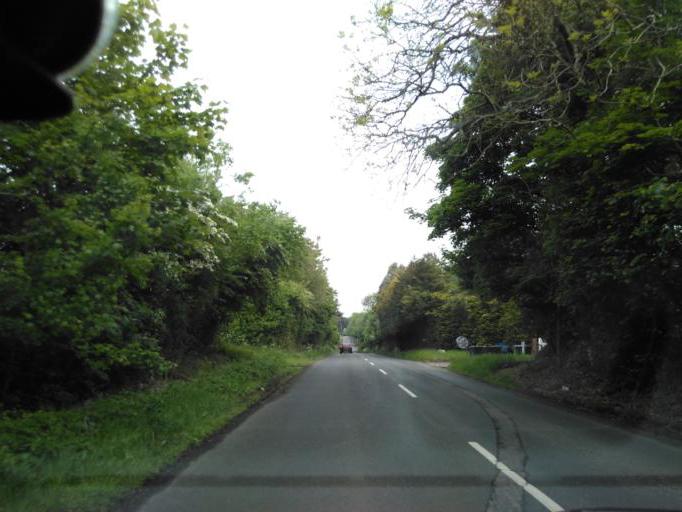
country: GB
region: England
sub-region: Kent
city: Lyminge
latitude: 51.1617
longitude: 1.0516
